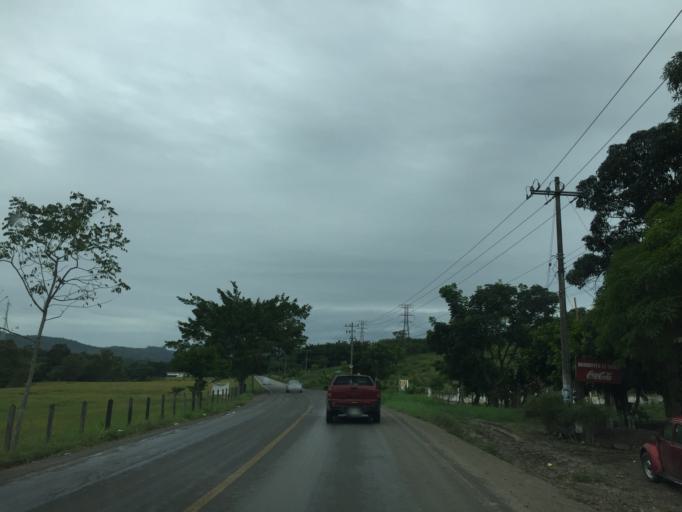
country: MX
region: Veracruz
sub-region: Papantla
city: El Chote
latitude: 20.4403
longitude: -97.4017
